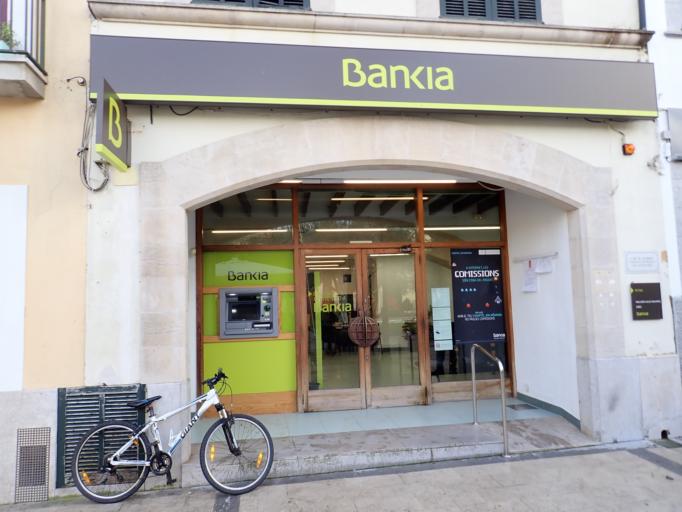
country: ES
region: Balearic Islands
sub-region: Illes Balears
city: Petra
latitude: 39.6141
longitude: 3.1126
